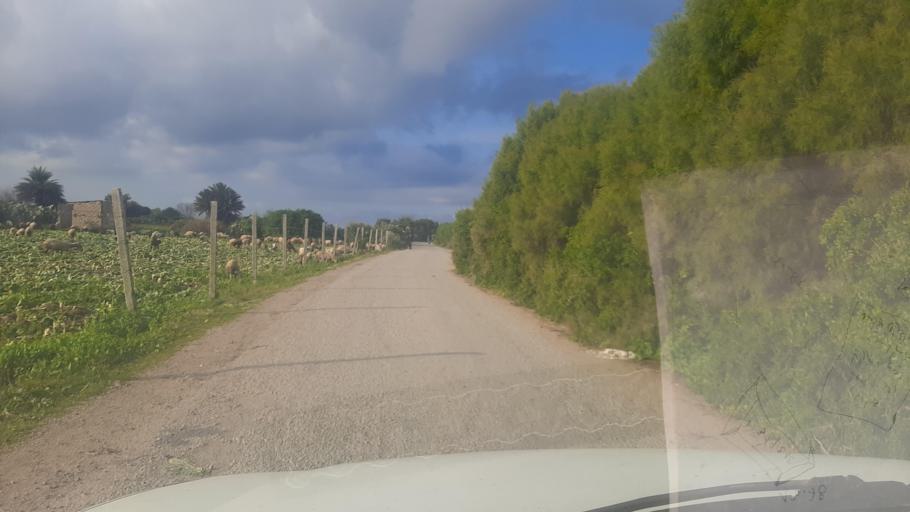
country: TN
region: Nabul
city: Manzil Bu Zalafah
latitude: 36.7103
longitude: 10.5010
